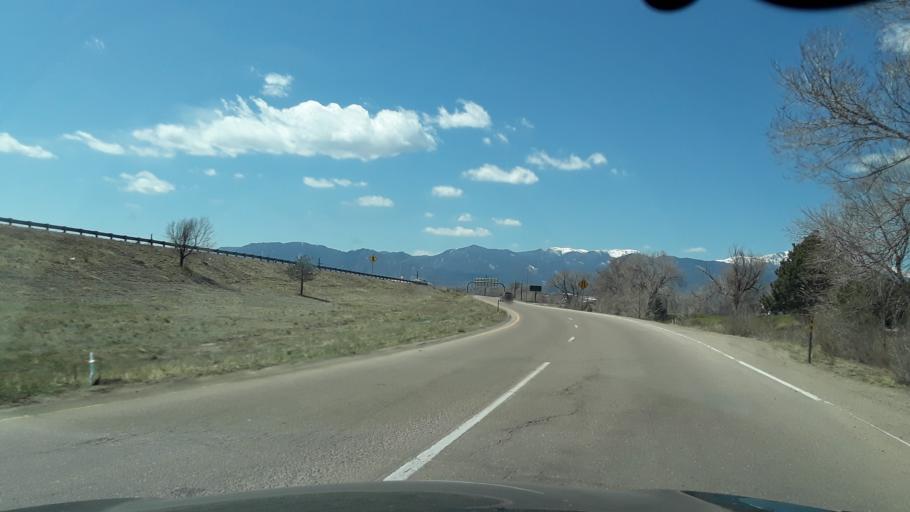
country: US
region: Colorado
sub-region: El Paso County
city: Cimarron Hills
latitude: 38.8400
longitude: -104.7017
